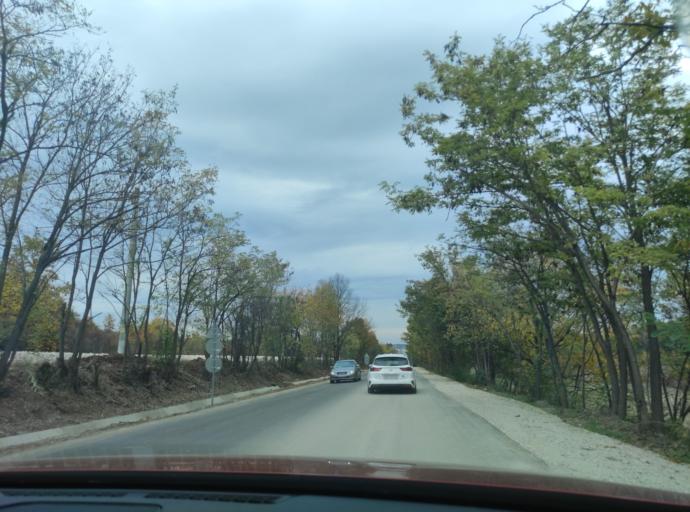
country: BG
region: Montana
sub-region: Obshtina Montana
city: Montana
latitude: 43.3870
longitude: 23.2431
